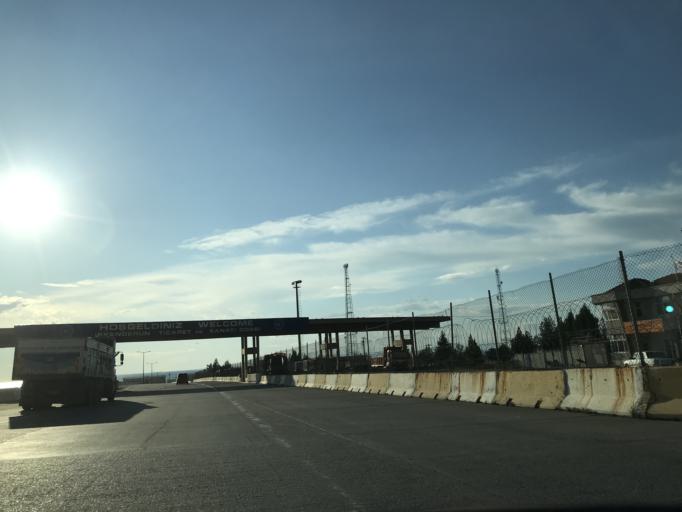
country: TR
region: Hatay
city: Guzelkoy
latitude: 36.6076
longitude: 36.2051
